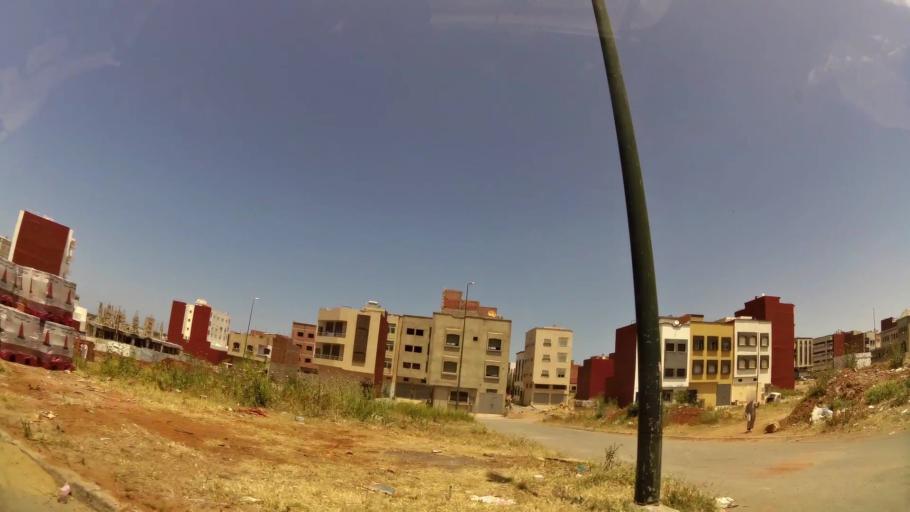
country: MA
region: Gharb-Chrarda-Beni Hssen
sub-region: Kenitra Province
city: Kenitra
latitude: 34.2650
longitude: -6.6247
